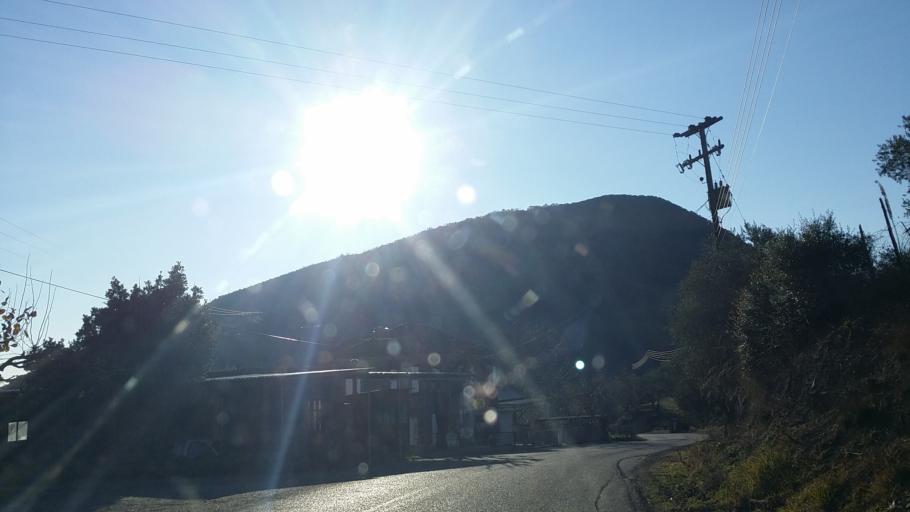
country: GR
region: West Greece
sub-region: Nomos Aitolias kai Akarnanias
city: Neapolis
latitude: 38.7955
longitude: 21.4519
